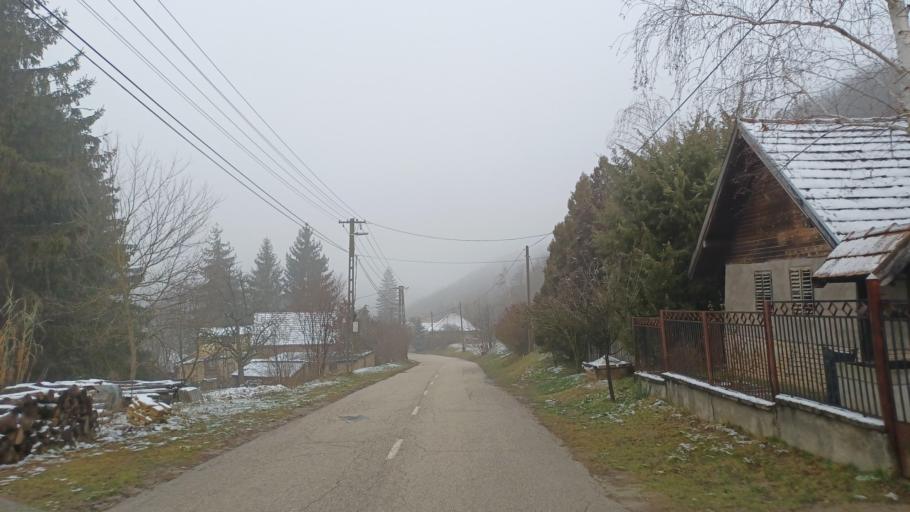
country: HU
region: Tolna
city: Pincehely
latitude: 46.6258
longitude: 18.4793
